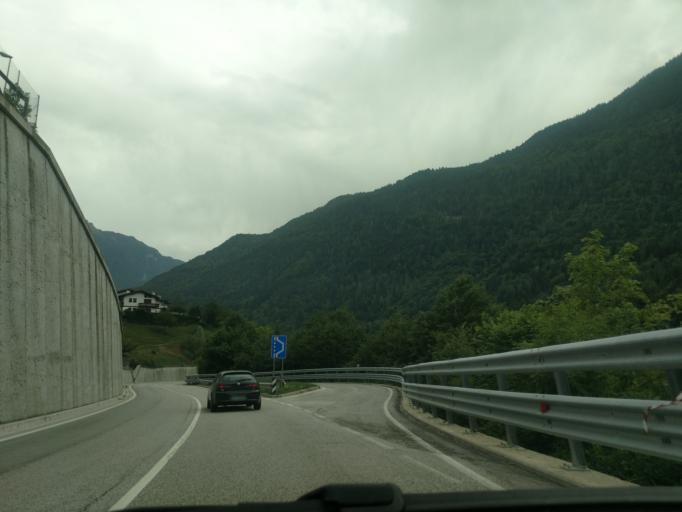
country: IT
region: Veneto
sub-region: Provincia di Belluno
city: Longarone
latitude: 46.2655
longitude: 12.2746
